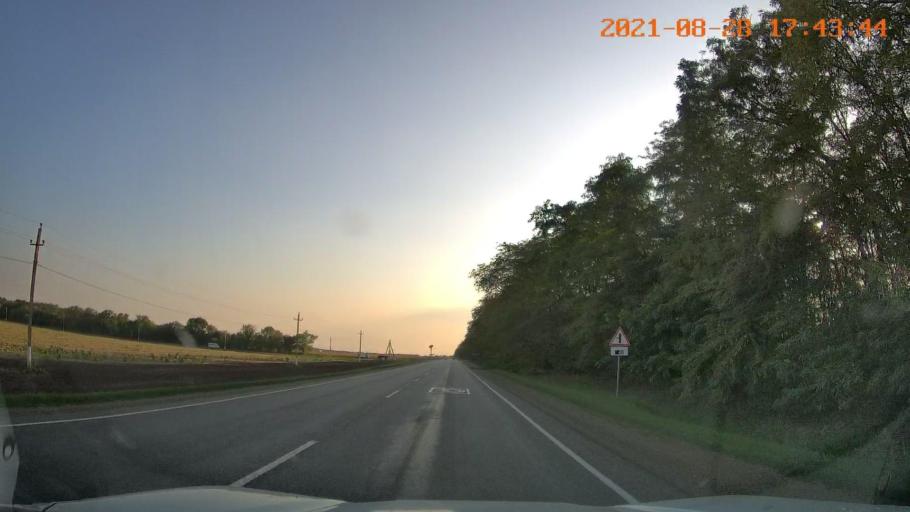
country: RU
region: Krasnodarskiy
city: Glubokiy
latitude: 45.0075
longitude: 40.9051
